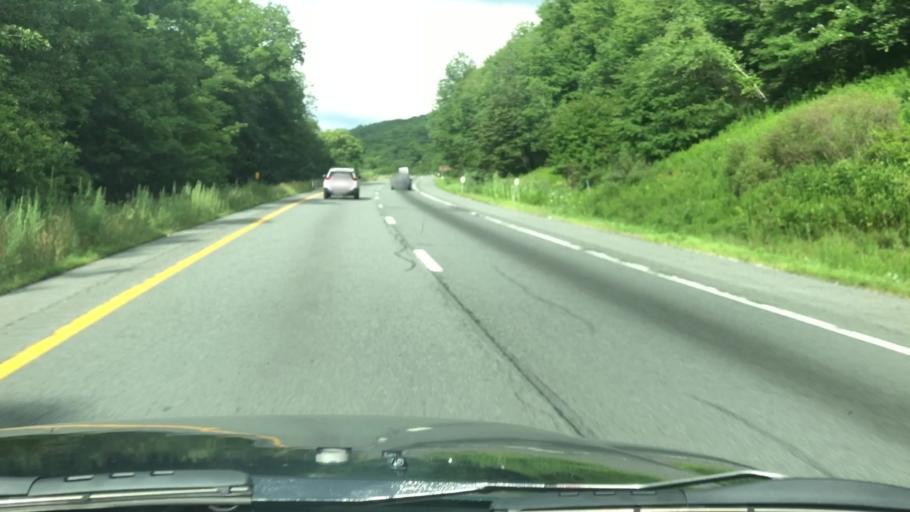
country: US
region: New York
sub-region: Orange County
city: Port Jervis
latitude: 41.3641
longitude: -74.6549
